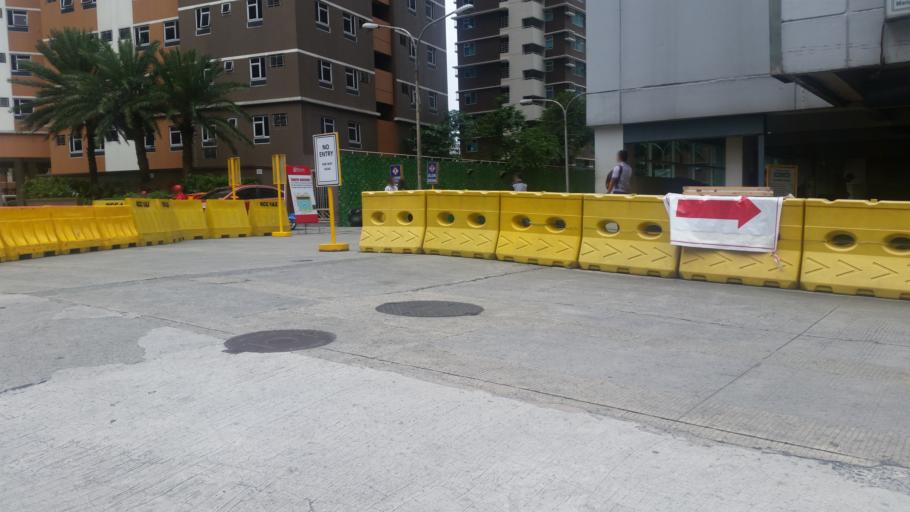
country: PH
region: Metro Manila
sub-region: Mandaluyong
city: Mandaluyong City
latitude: 14.5717
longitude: 121.0487
